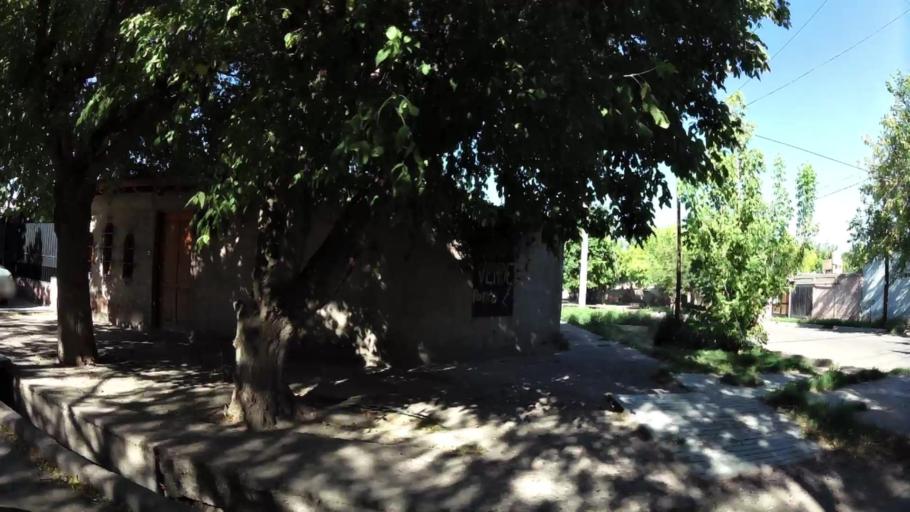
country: AR
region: Mendoza
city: Las Heras
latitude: -32.8383
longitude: -68.8296
